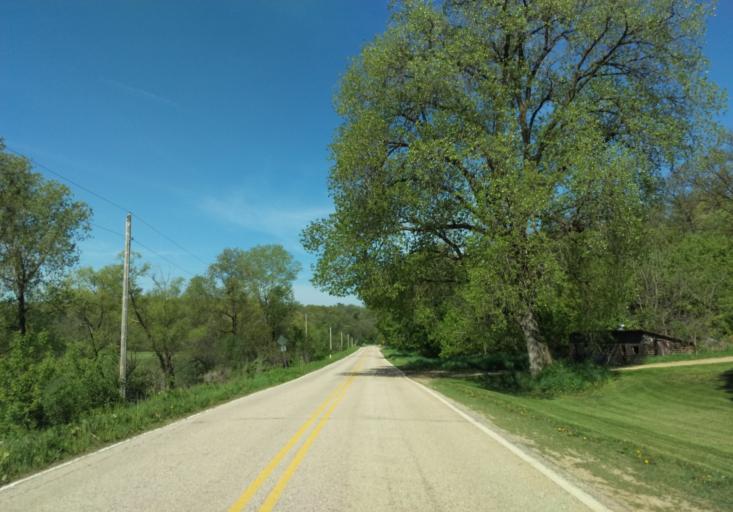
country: US
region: Wisconsin
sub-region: Dane County
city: Mount Horeb
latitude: 43.0586
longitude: -89.7769
